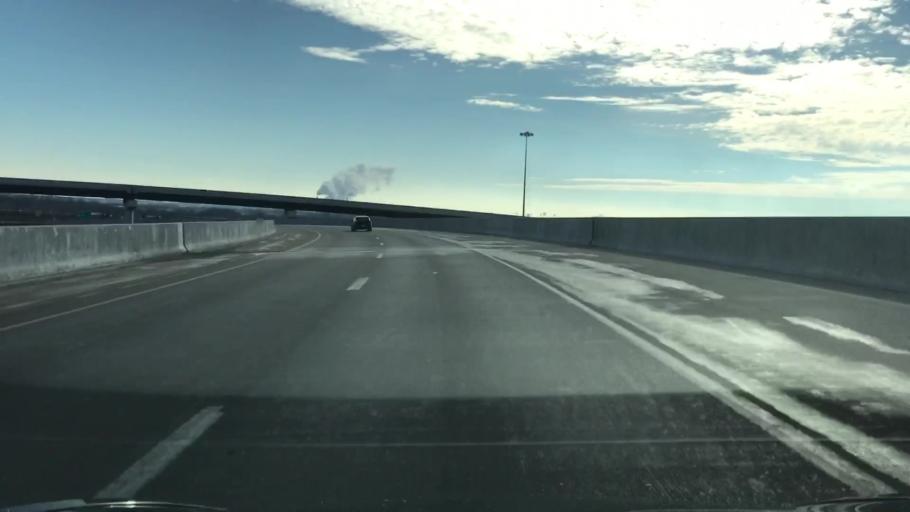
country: US
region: Nebraska
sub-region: Douglas County
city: Omaha
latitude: 41.2336
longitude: -95.8986
